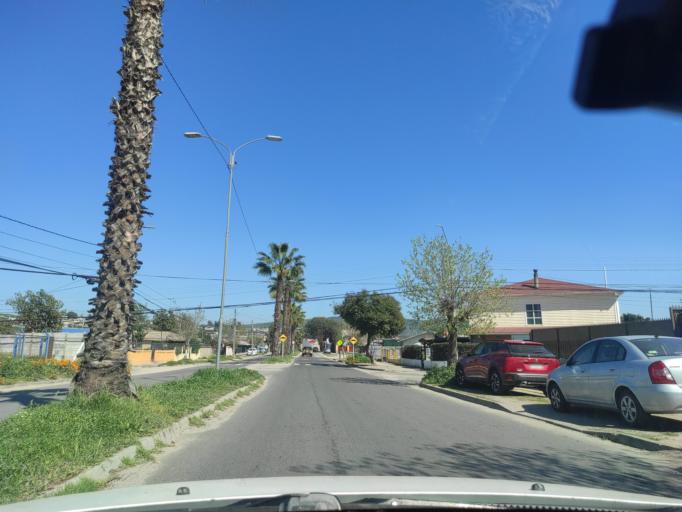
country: CL
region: Valparaiso
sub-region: Provincia de Marga Marga
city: Limache
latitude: -33.0147
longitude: -71.2544
